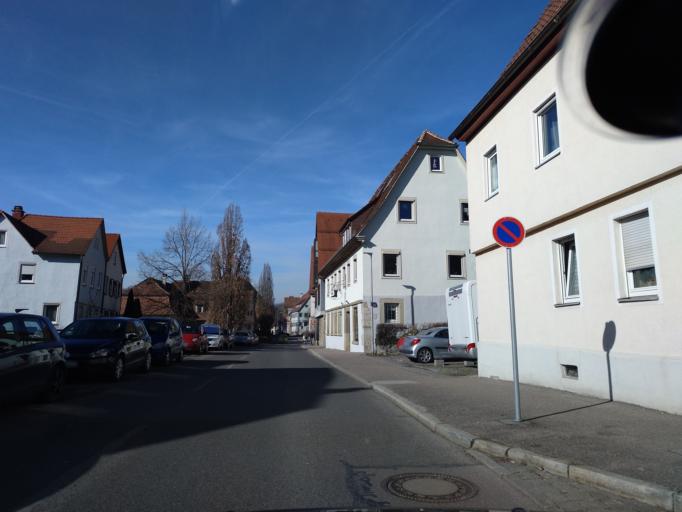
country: DE
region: Baden-Wuerttemberg
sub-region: Regierungsbezirk Stuttgart
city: Schwaebisch Hall
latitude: 49.1079
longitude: 9.7408
